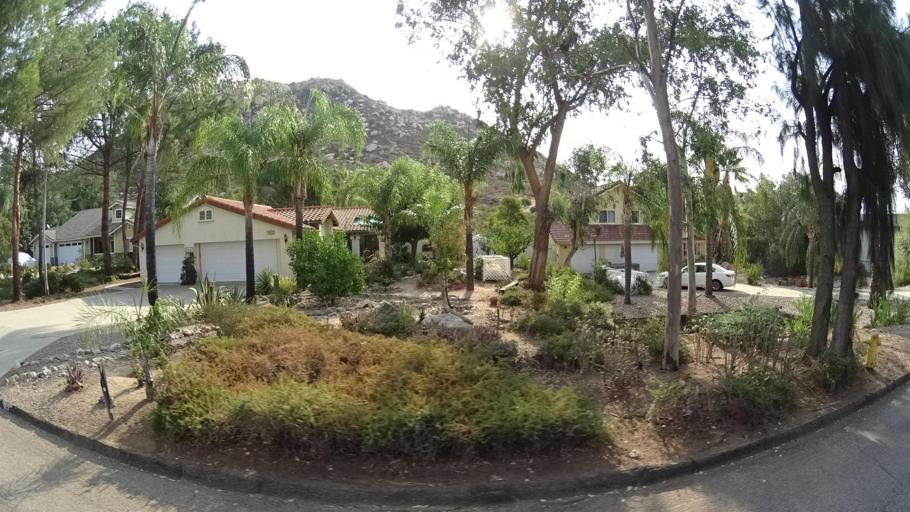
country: US
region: California
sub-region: San Diego County
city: San Diego Country Estates
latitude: 33.0149
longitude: -116.7894
